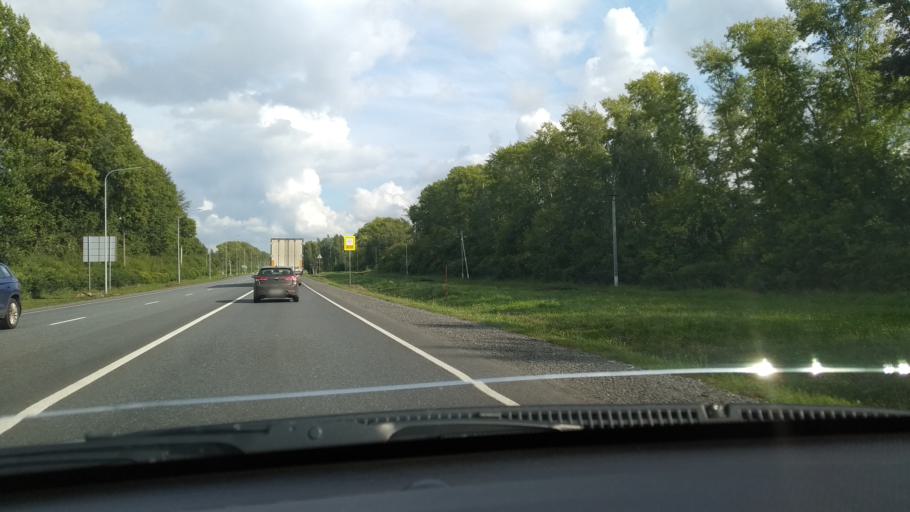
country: RU
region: Tatarstan
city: Stolbishchi
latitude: 55.6540
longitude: 49.3166
